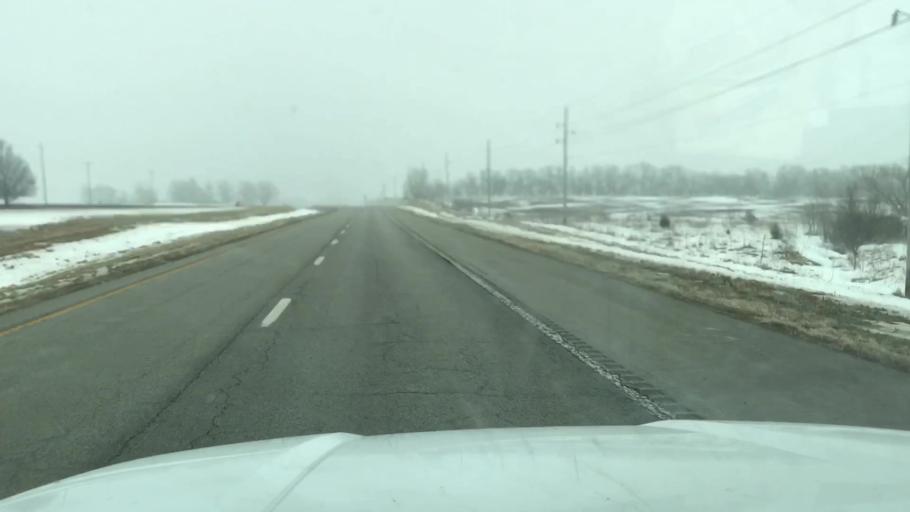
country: US
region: Missouri
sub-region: Clinton County
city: Cameron
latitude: 39.7543
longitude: -94.3327
